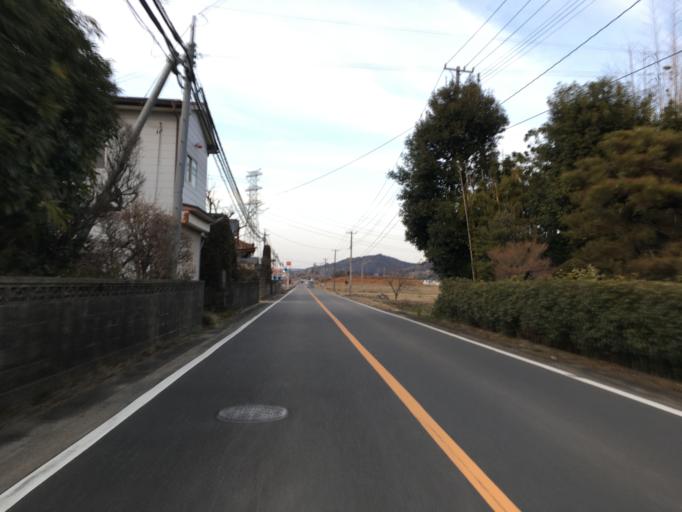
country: JP
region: Ibaraki
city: Daigo
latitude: 36.9229
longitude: 140.4079
